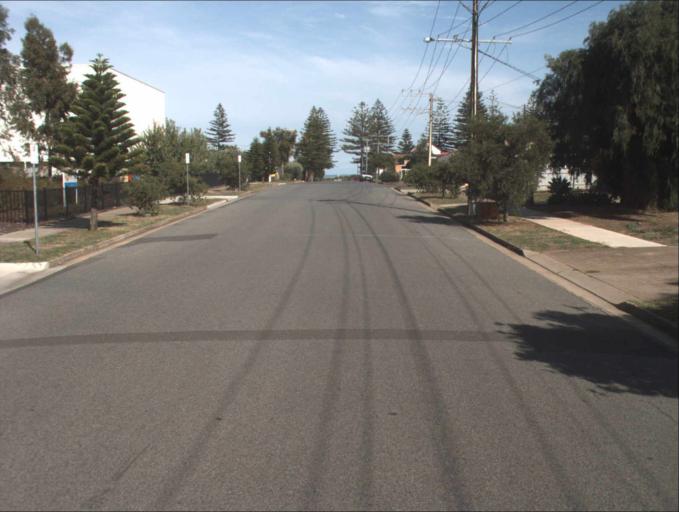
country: AU
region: South Australia
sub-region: Port Adelaide Enfield
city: Birkenhead
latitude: -34.8010
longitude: 138.4947
